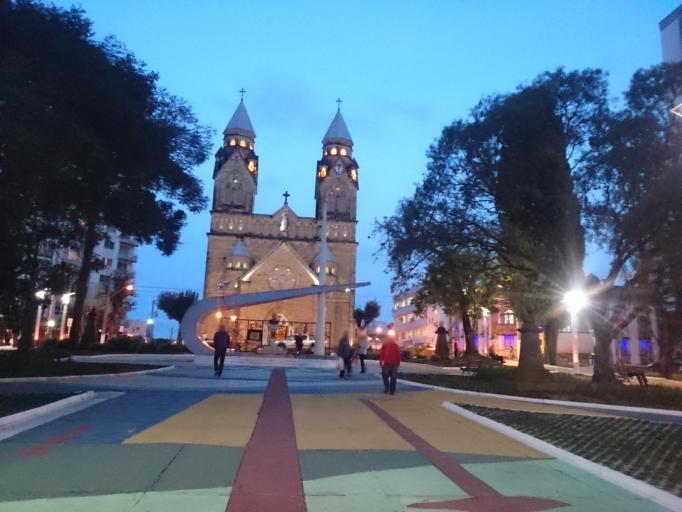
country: BR
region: Santa Catarina
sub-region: Lages
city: Lages
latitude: -27.8163
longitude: -50.3261
